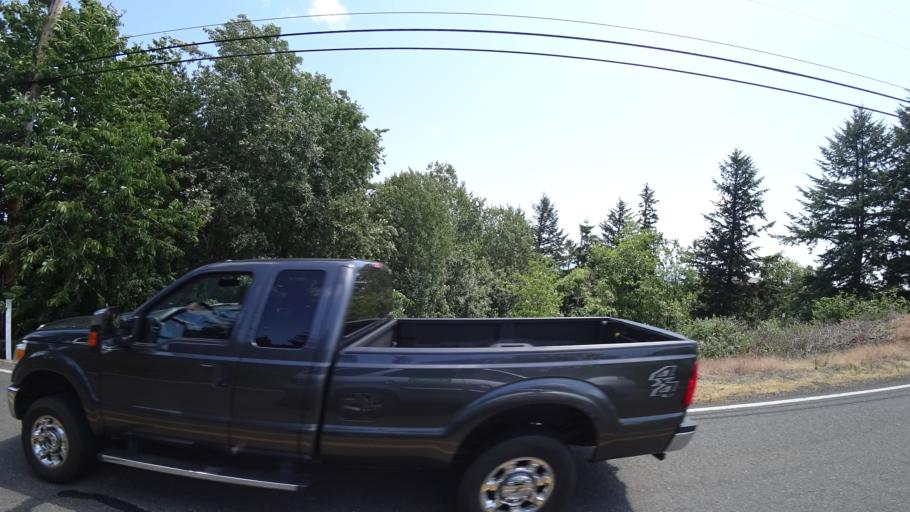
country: US
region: Oregon
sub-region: Clackamas County
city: Happy Valley
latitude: 45.4519
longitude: -122.5418
